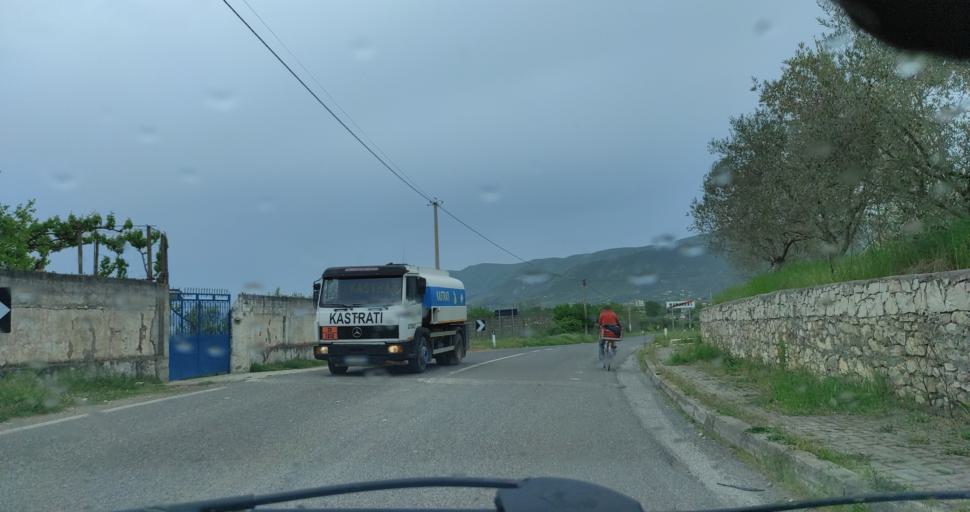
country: AL
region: Lezhe
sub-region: Rrethi i Kurbinit
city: Mamurras
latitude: 41.5875
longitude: 19.6929
